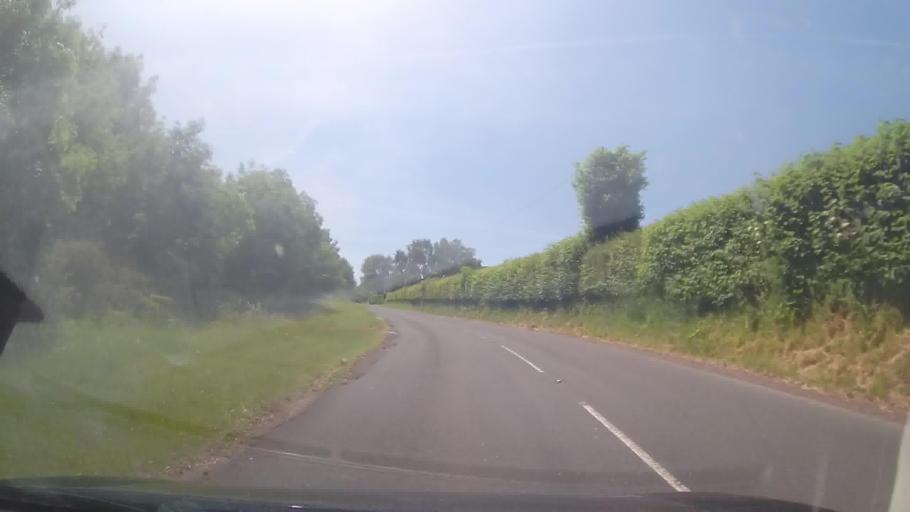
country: GB
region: England
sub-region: Herefordshire
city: Llanrothal
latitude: 51.8818
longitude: -2.7334
